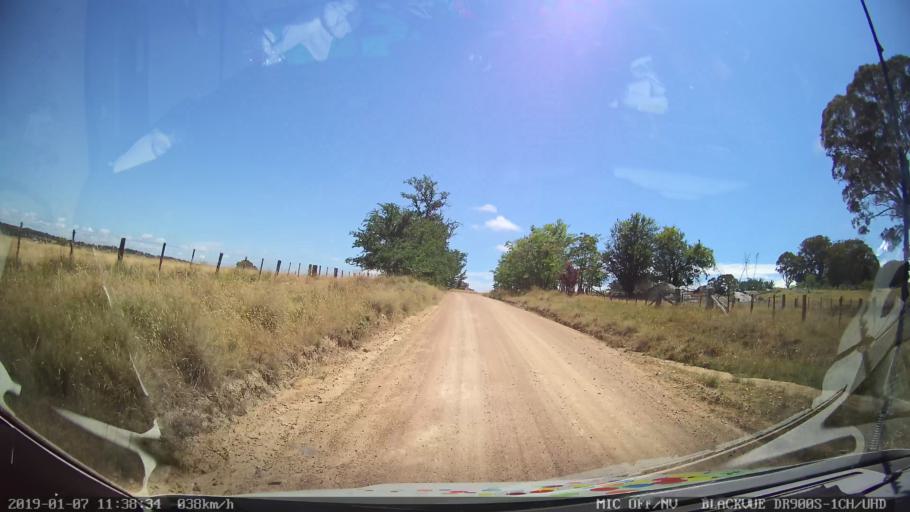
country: AU
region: New South Wales
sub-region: Armidale Dumaresq
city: Armidale
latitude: -30.3707
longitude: 151.5725
